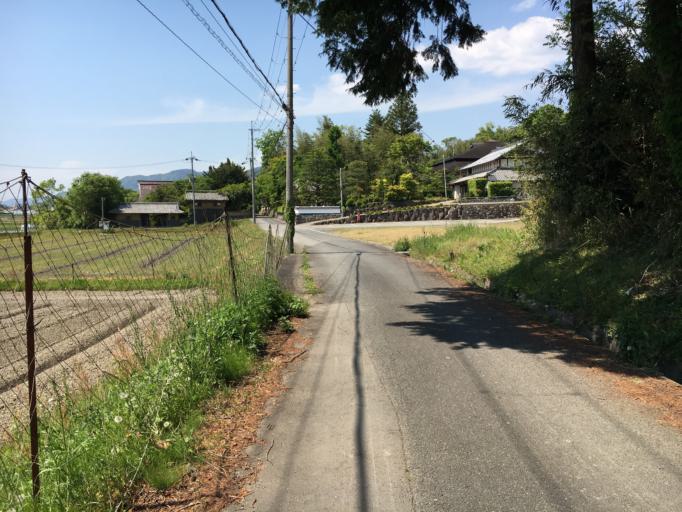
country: JP
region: Kyoto
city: Kameoka
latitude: 35.0716
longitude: 135.5694
